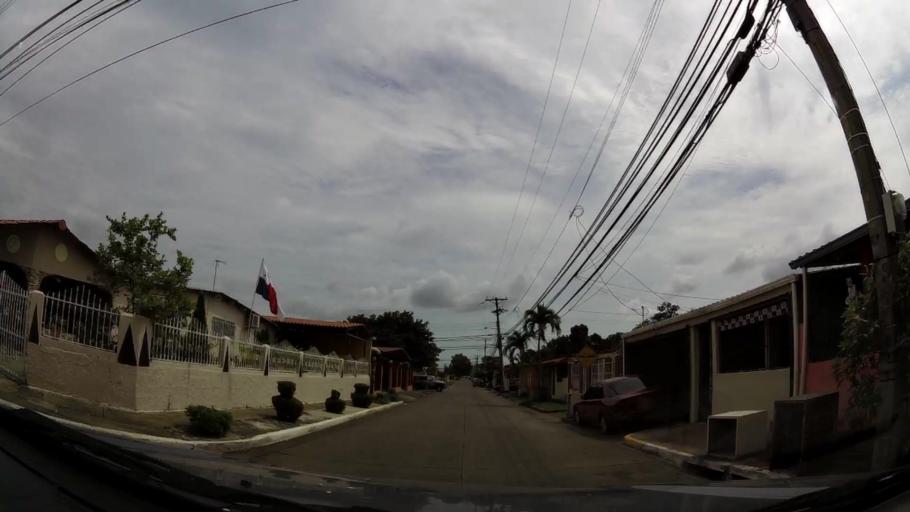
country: PA
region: Panama
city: San Miguelito
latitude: 9.0500
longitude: -79.4223
